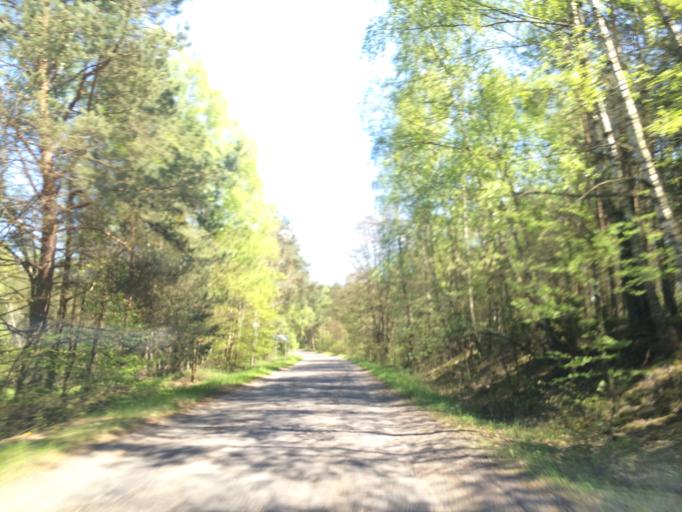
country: PL
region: Warmian-Masurian Voivodeship
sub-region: Powiat nowomiejski
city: Kurzetnik
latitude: 53.3822
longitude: 19.4865
